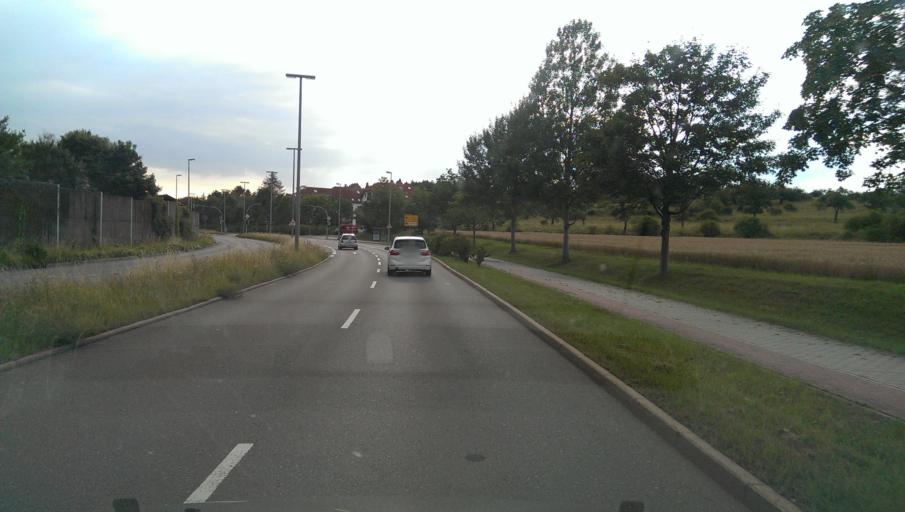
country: DE
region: Thuringia
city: Gera
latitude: 50.8816
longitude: 12.1128
